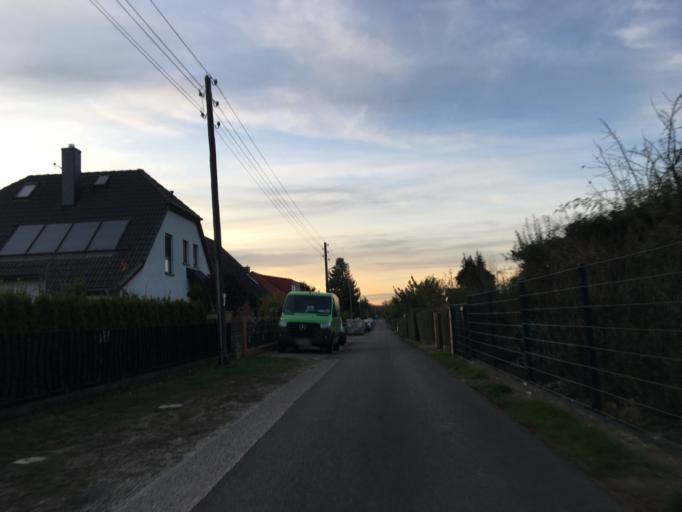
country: DE
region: Berlin
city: Buchholz
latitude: 52.6177
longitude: 13.4250
